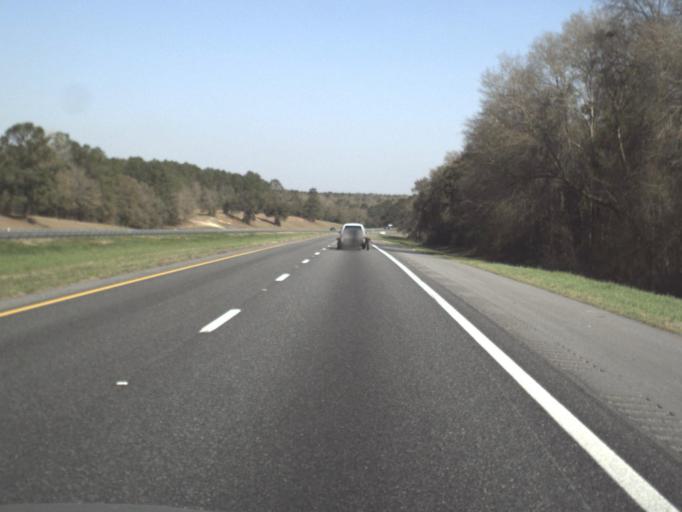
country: US
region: Florida
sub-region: Gadsden County
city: Gretna
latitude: 30.6107
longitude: -84.7517
